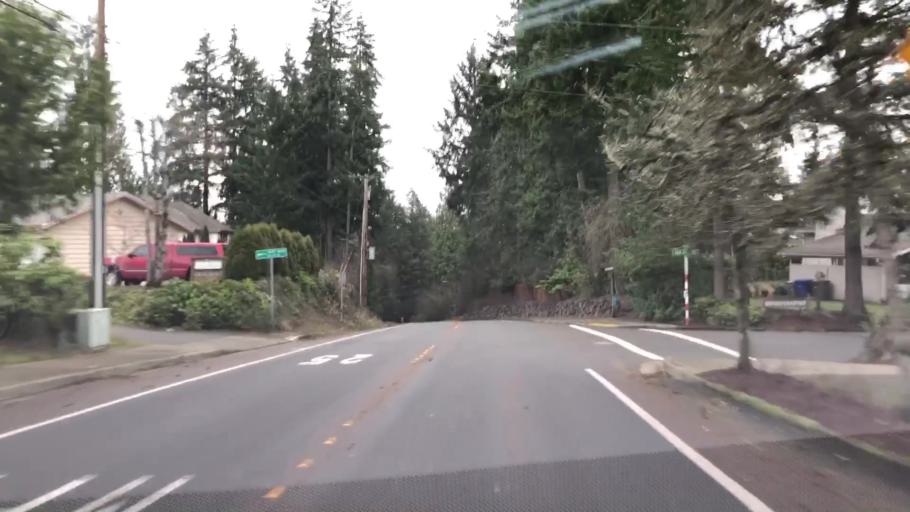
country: US
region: Washington
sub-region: King County
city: West Lake Sammamish
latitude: 47.5890
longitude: -122.1187
